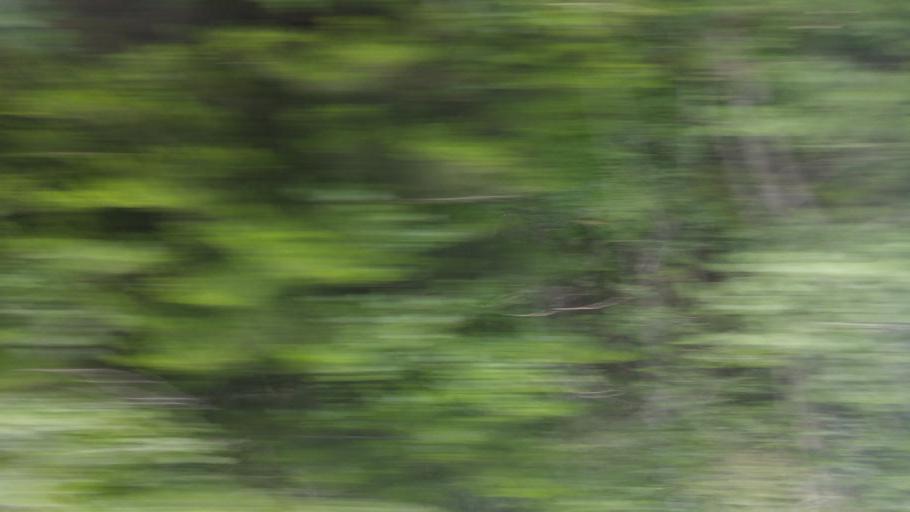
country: NO
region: Sor-Trondelag
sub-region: Midtre Gauldal
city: Storen
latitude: 63.0006
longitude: 10.4656
